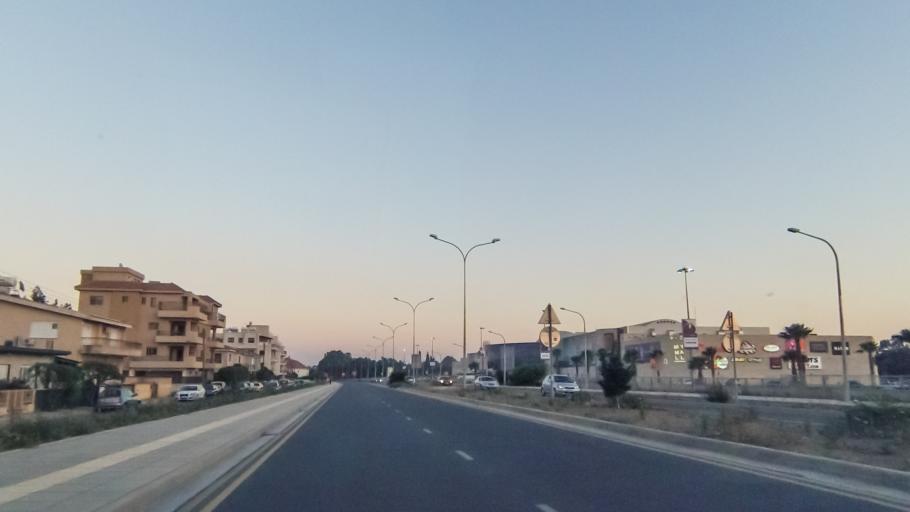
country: CY
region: Limassol
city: Ypsonas
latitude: 34.6556
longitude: 32.9974
